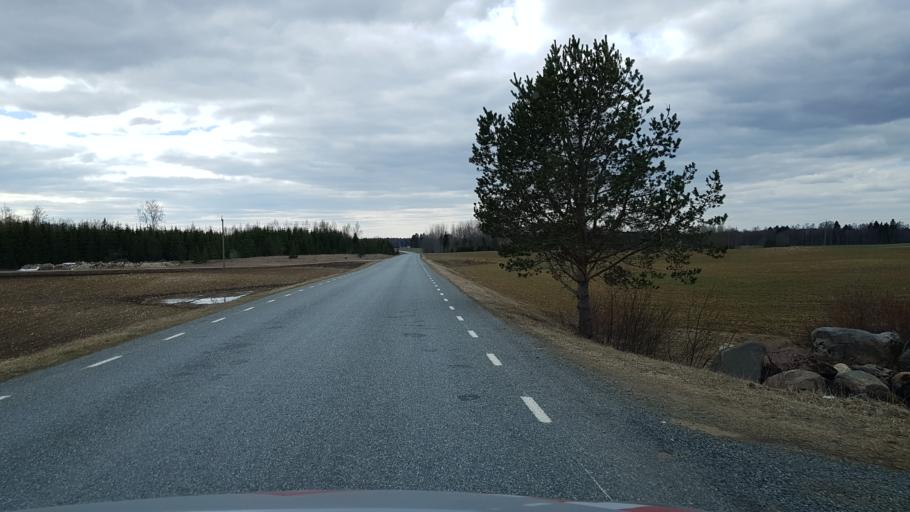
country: EE
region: Laeaene-Virumaa
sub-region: Rakvere linn
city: Rakvere
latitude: 59.2669
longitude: 26.2697
